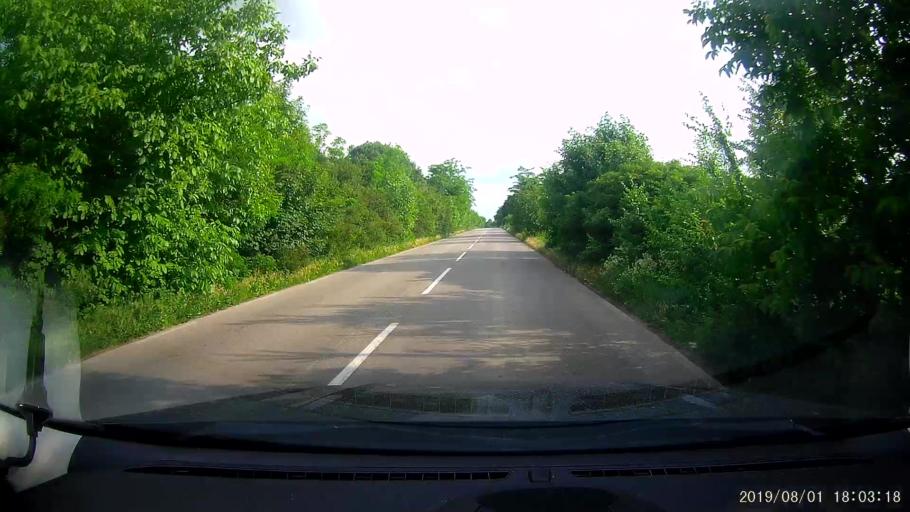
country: BG
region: Silistra
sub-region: Obshtina Alfatar
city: Alfatar
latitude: 43.9307
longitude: 27.2899
